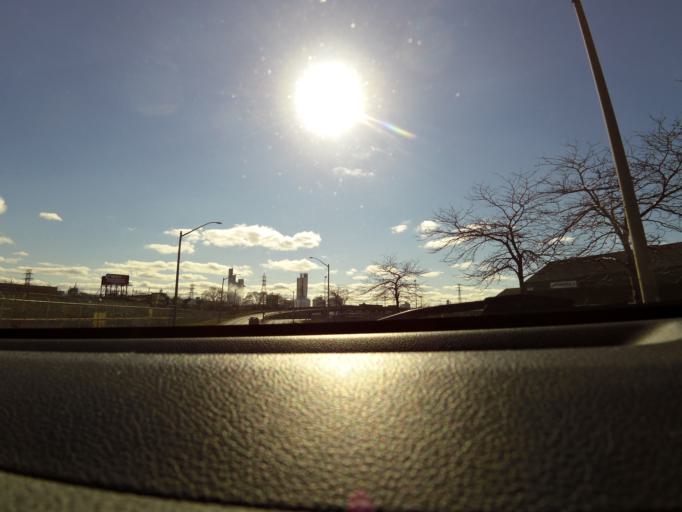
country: CA
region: Ontario
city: Hamilton
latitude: 43.2648
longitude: -79.8232
